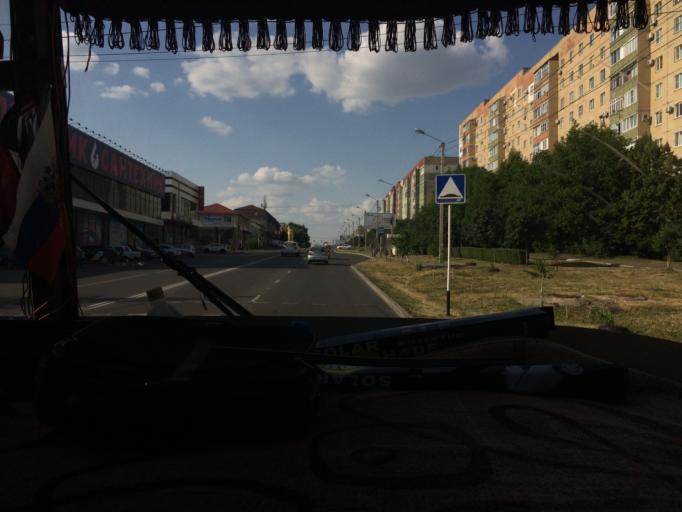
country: RU
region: Stavropol'skiy
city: Tatarka
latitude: 45.0035
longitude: 41.9115
